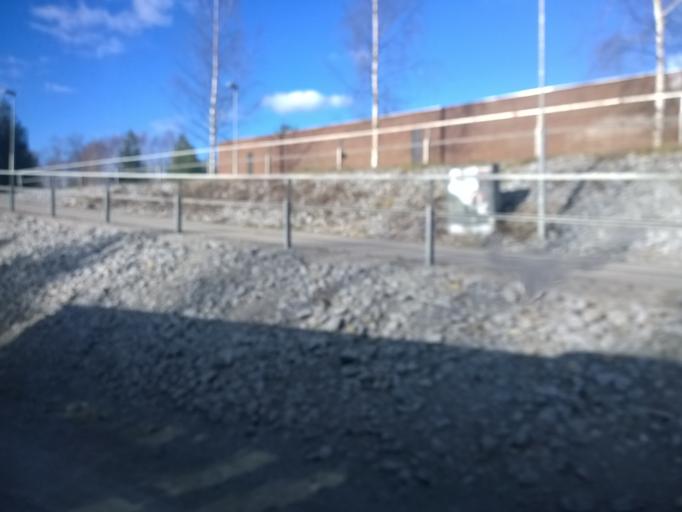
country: FI
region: Pirkanmaa
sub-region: Tampere
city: Tampere
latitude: 61.4767
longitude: 23.8346
